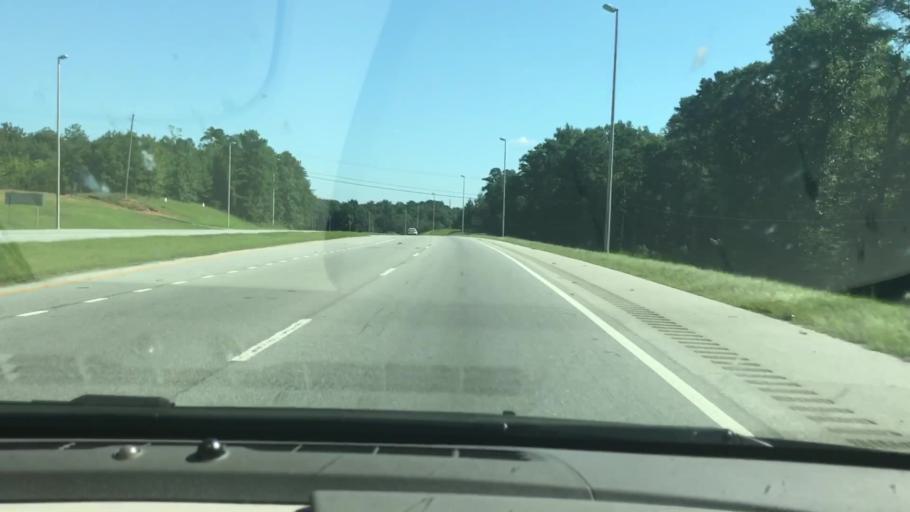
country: US
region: Alabama
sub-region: Russell County
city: Phenix City
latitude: 32.4305
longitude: -85.0295
